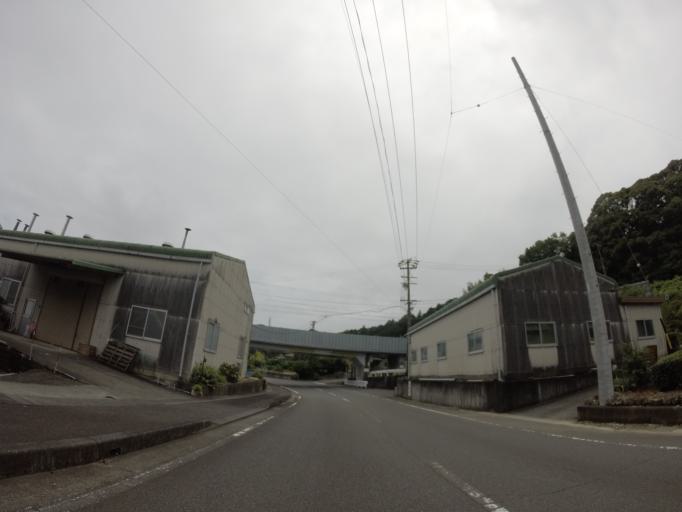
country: JP
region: Shizuoka
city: Kanaya
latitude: 34.7880
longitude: 138.1497
